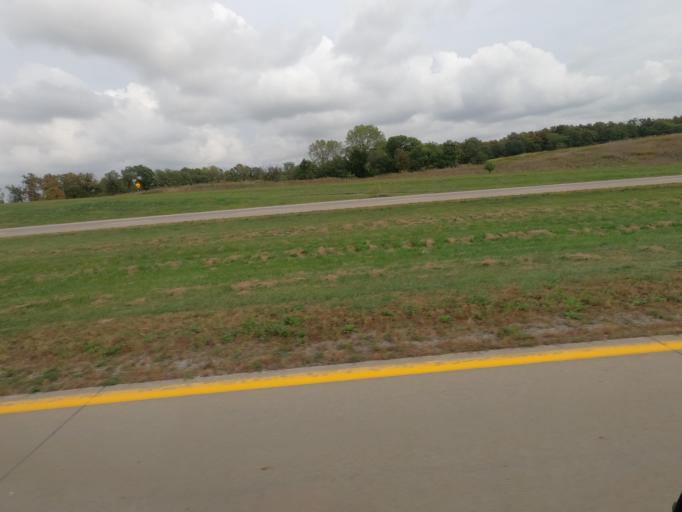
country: US
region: Iowa
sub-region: Wapello County
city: Ottumwa
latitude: 41.0488
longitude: -92.3728
